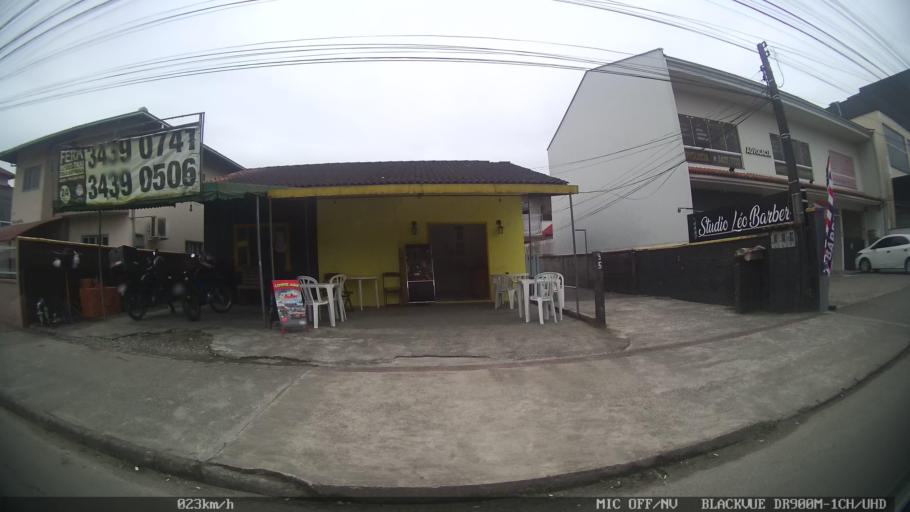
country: BR
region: Santa Catarina
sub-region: Joinville
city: Joinville
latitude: -26.2865
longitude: -48.9024
